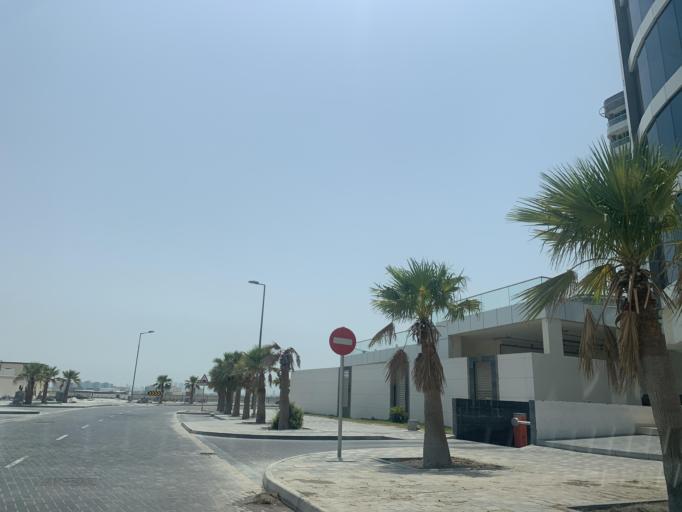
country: BH
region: Muharraq
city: Al Hadd
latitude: 26.2691
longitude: 50.6774
